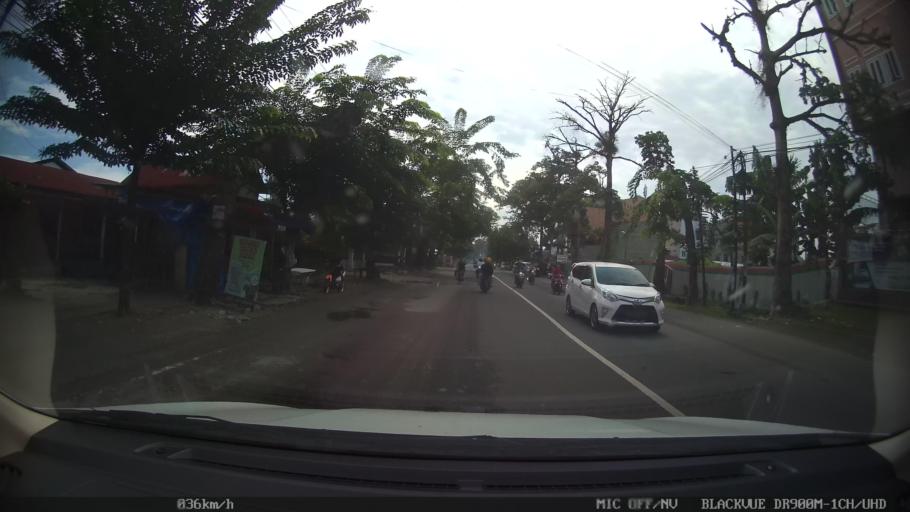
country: ID
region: North Sumatra
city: Medan
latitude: 3.6226
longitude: 98.6887
